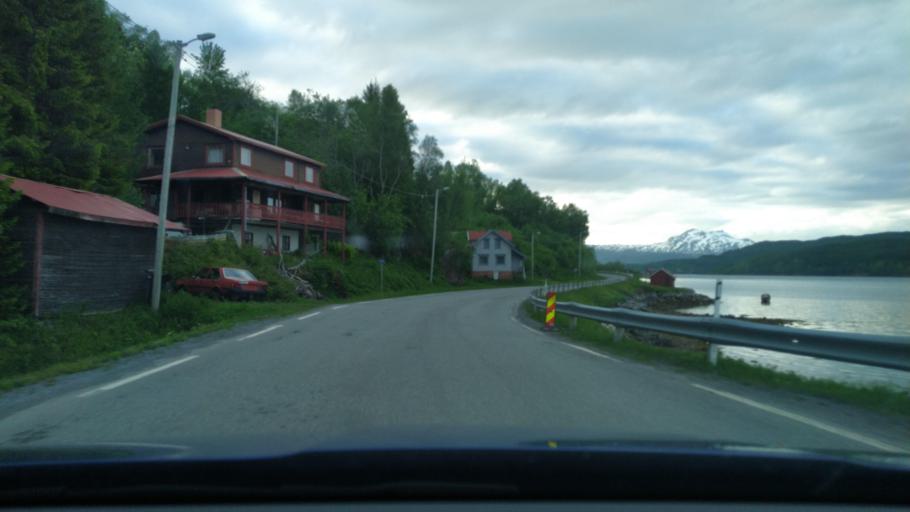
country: NO
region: Troms
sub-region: Sorreisa
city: Sorreisa
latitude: 69.1398
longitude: 18.0577
